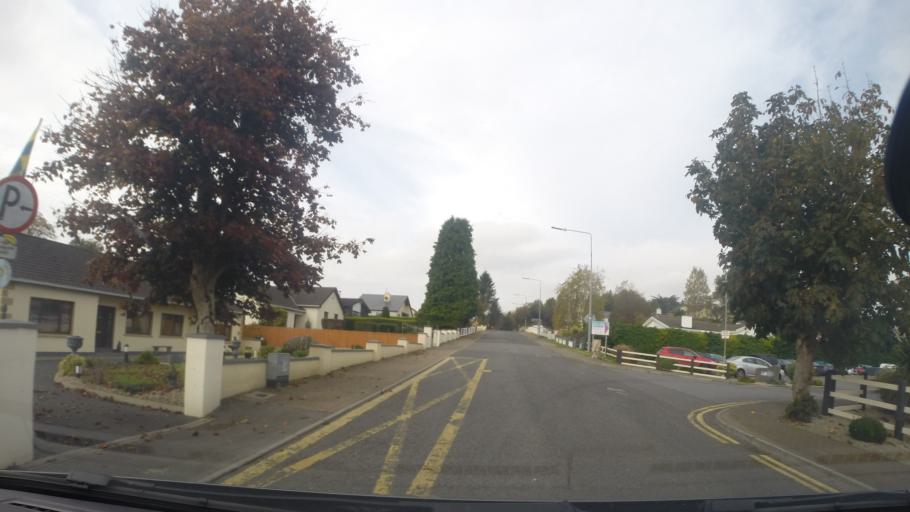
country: IE
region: Connaught
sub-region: County Leitrim
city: Manorhamilton
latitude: 54.3069
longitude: -8.1755
